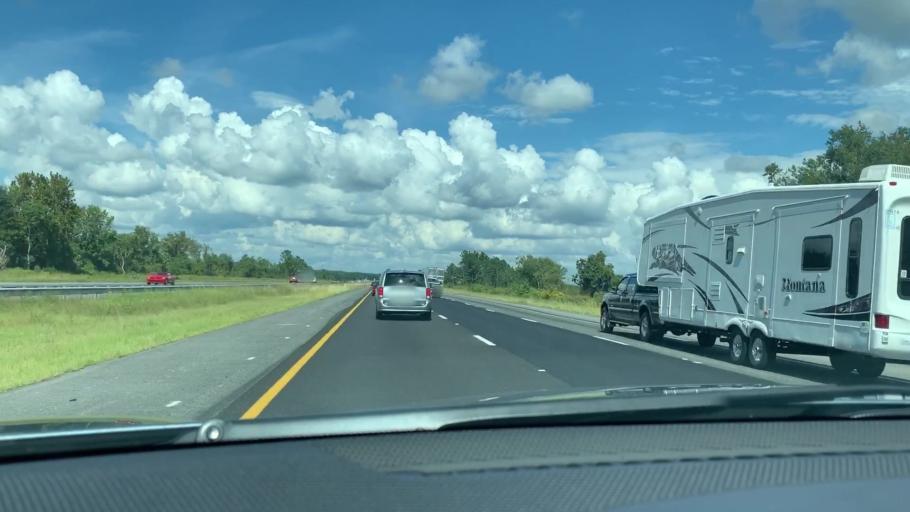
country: US
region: Georgia
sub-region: Camden County
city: Woodbine
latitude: 31.0249
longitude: -81.6565
